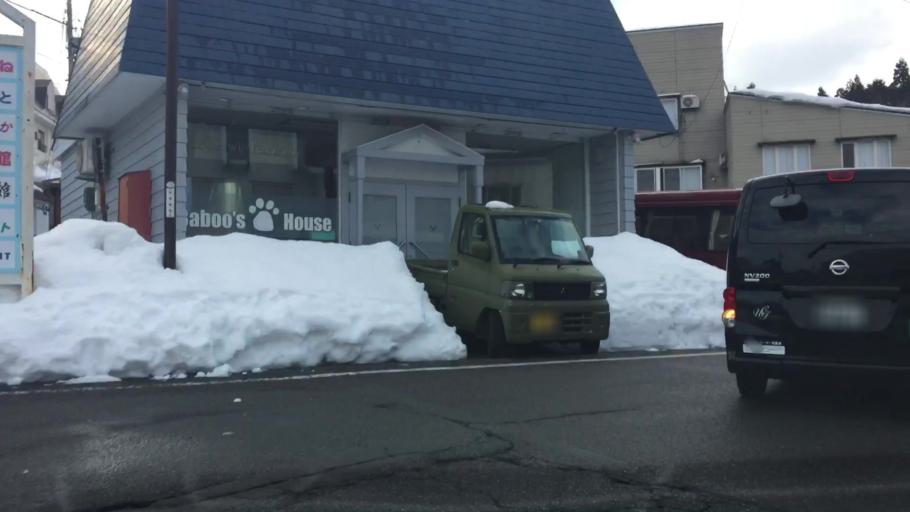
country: JP
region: Niigata
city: Shiozawa
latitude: 36.9902
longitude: 138.8228
